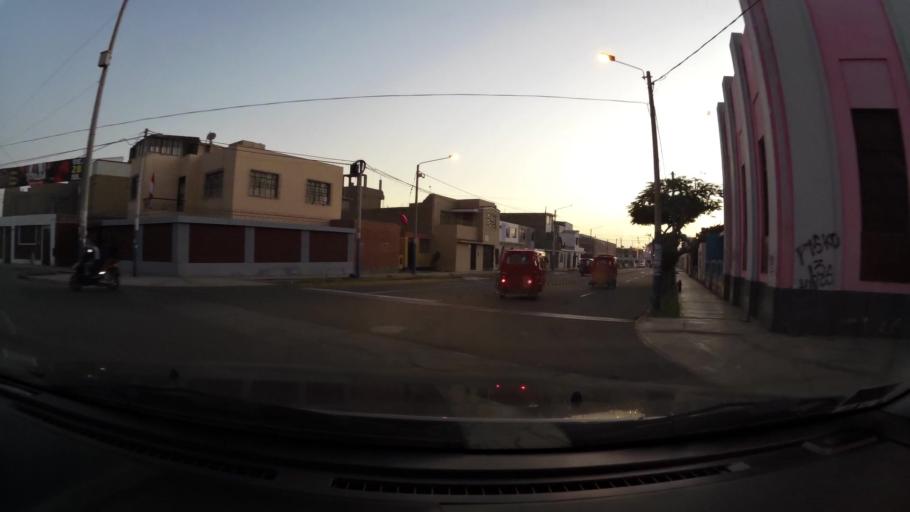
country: PE
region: Ica
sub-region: Provincia de Pisco
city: Pisco
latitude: -13.7097
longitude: -76.2099
